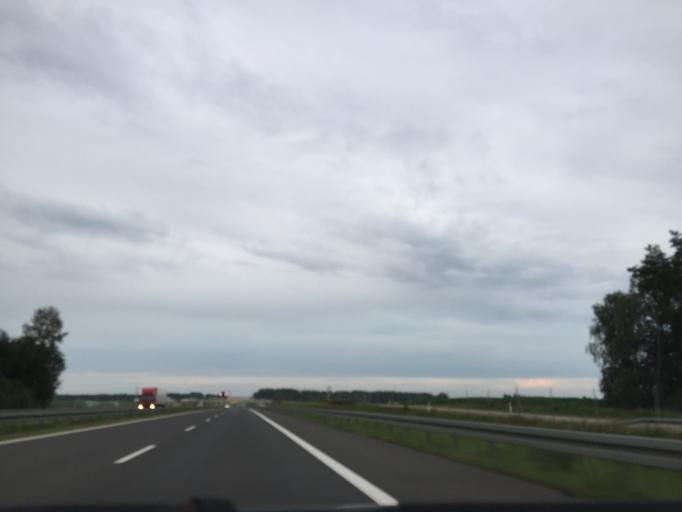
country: PL
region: Podlasie
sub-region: Powiat bialostocki
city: Tykocin
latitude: 53.1395
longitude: 22.7699
